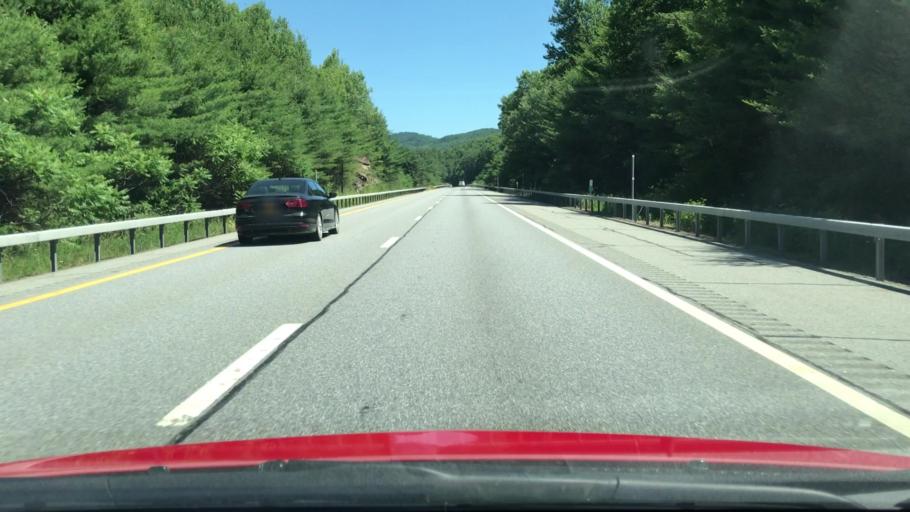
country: US
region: New York
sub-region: Warren County
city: Warrensburg
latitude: 43.5381
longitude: -73.7382
